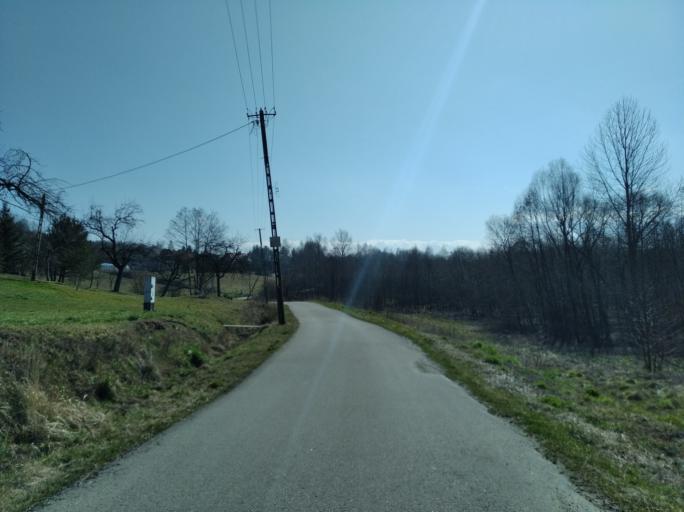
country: PL
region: Subcarpathian Voivodeship
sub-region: Powiat strzyzowski
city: Wysoka Strzyzowska
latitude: 49.8442
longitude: 21.7371
